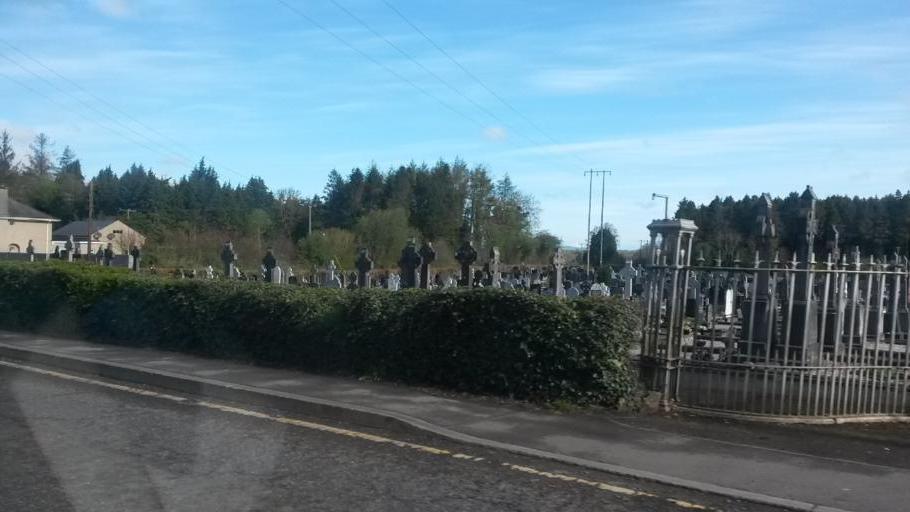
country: IE
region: Leinster
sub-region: An Mhi
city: Kells
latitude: 53.7246
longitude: -6.8642
